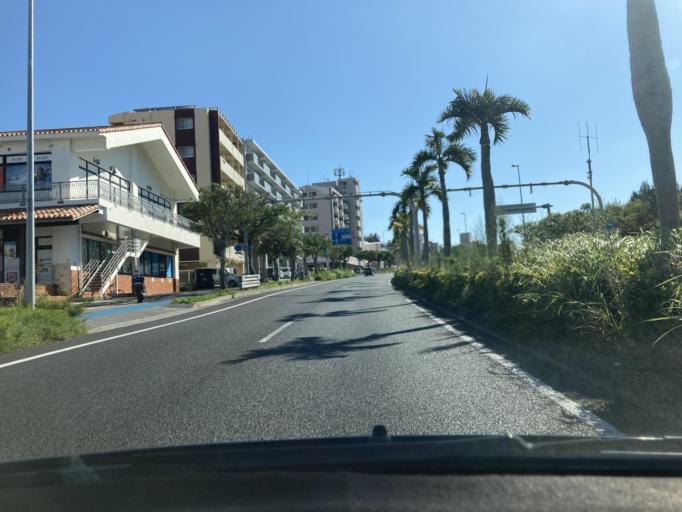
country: JP
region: Okinawa
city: Naha-shi
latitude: 26.2007
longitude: 127.6619
